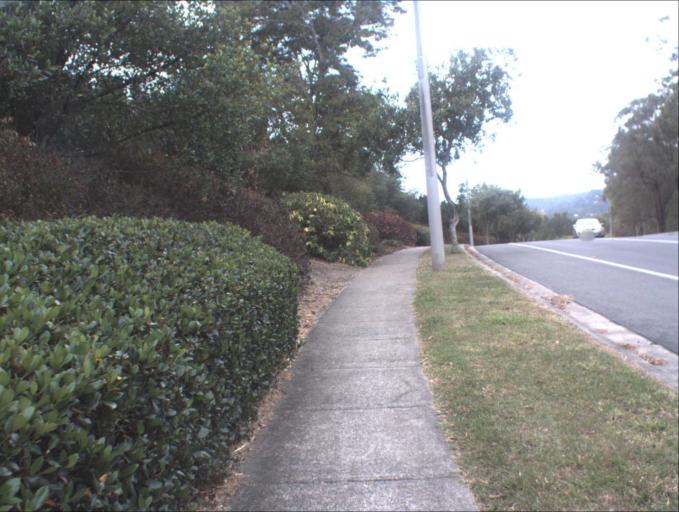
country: AU
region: Queensland
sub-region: Logan
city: Beenleigh
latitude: -27.6793
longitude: 153.1803
